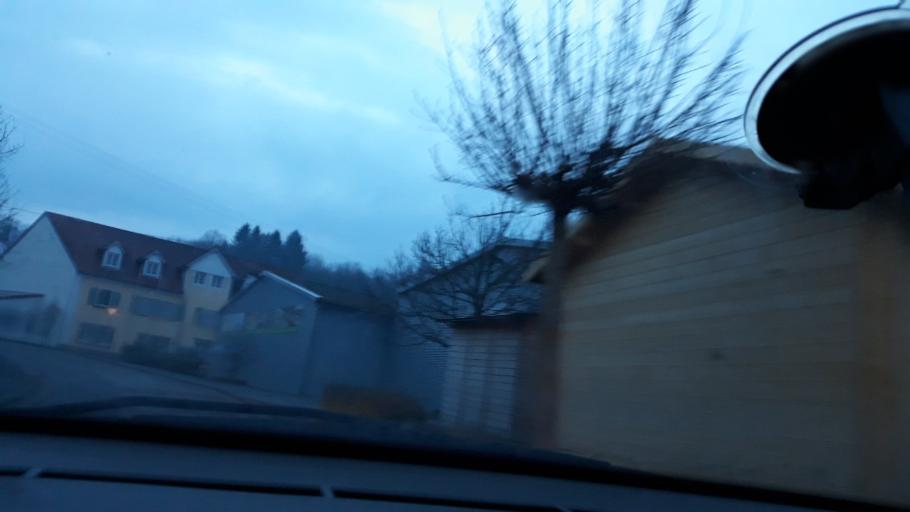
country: DE
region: Saarland
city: Blieskastel
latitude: 49.2158
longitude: 7.2555
